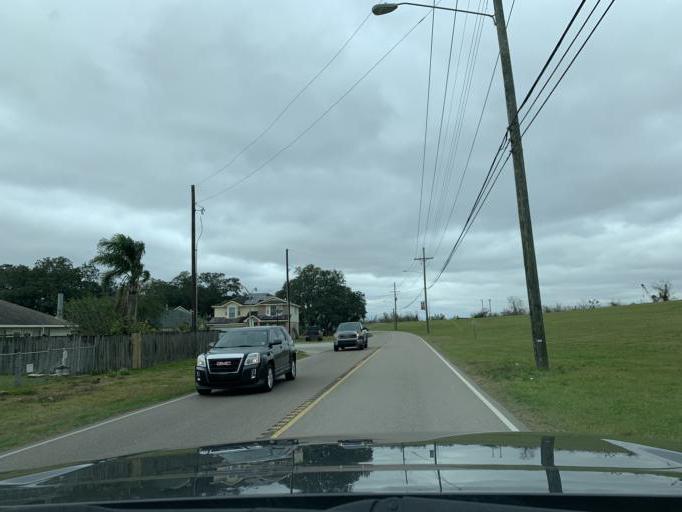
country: US
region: Louisiana
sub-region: Jefferson Parish
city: River Ridge
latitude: 29.9521
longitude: -90.2331
